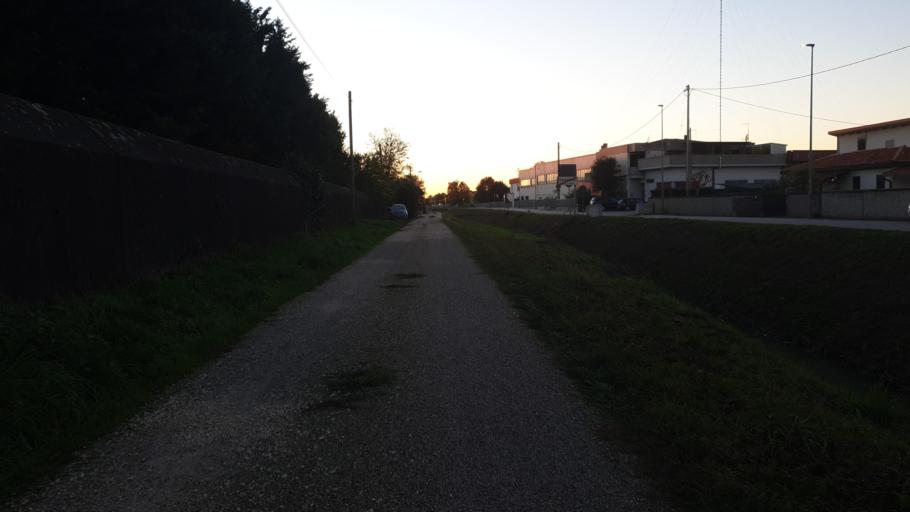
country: IT
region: Veneto
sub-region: Provincia di Venezia
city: Cazzago-Ex Polo
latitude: 45.4435
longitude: 12.0681
